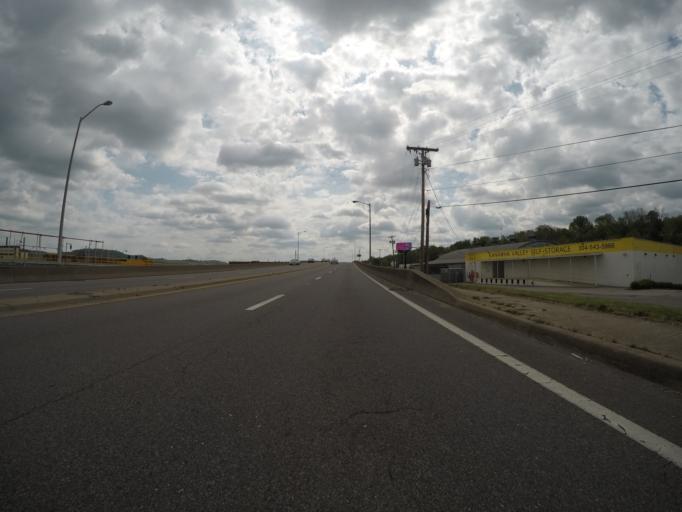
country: US
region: West Virginia
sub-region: Kanawha County
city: South Charleston
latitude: 38.3667
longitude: -81.6830
